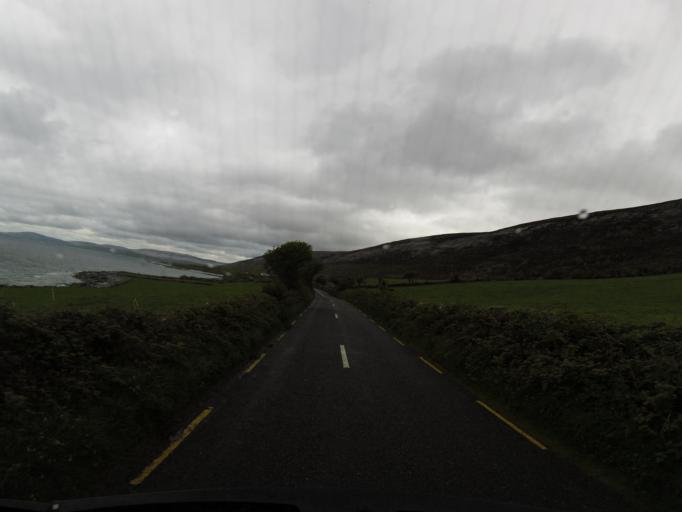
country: IE
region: Connaught
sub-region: County Galway
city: Bearna
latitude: 53.1440
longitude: -9.2332
